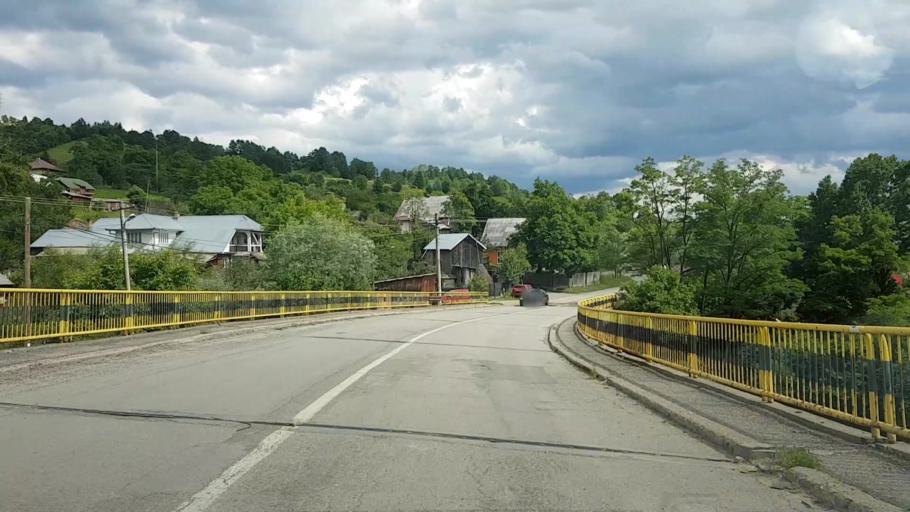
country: RO
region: Neamt
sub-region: Comuna Hangu
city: Hangu
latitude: 47.0443
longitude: 26.0536
